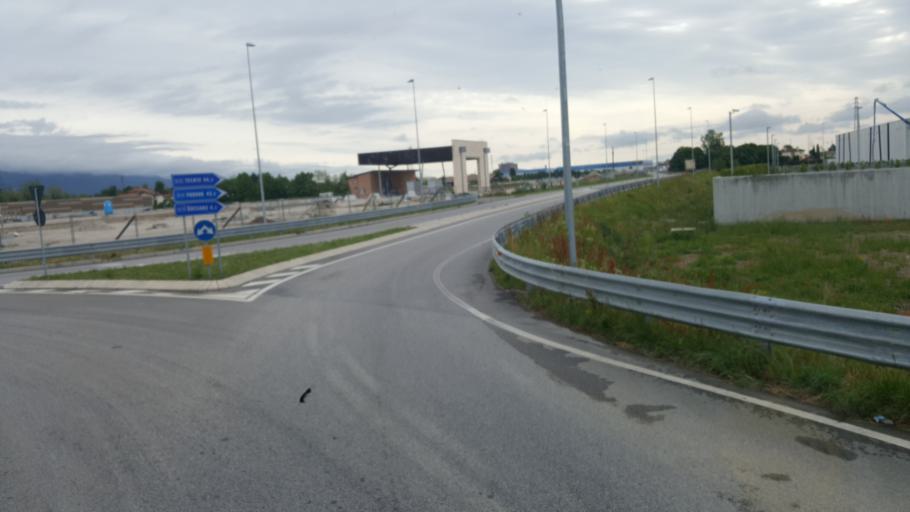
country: IT
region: Veneto
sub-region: Provincia di Vicenza
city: Bassano del Grappa
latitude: 45.7370
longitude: 11.7153
